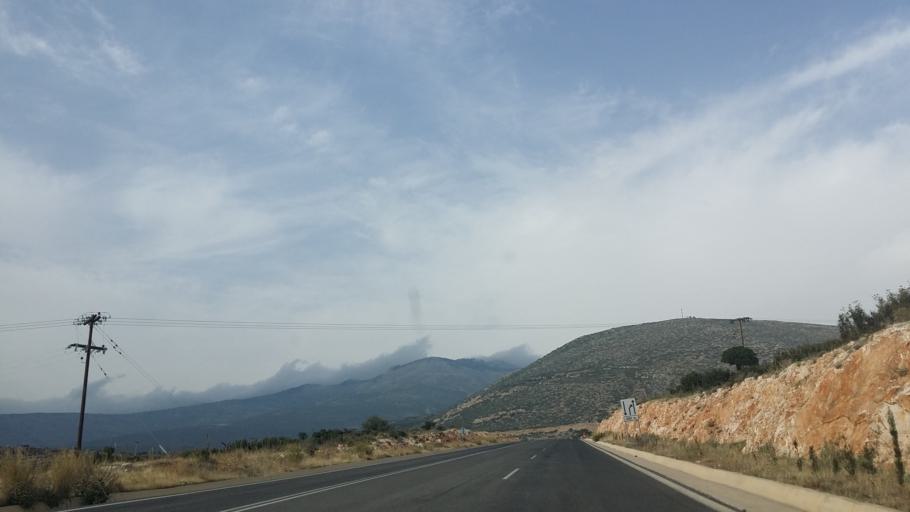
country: GR
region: Central Greece
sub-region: Nomos Voiotias
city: Korini
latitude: 38.2507
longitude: 22.9905
